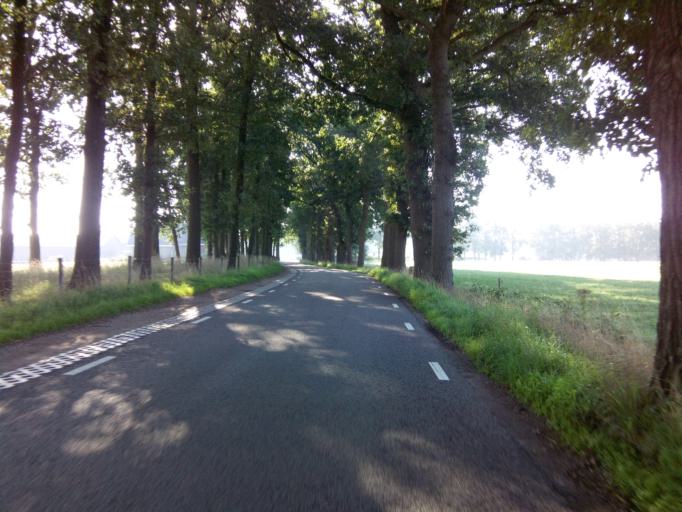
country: NL
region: Utrecht
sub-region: Gemeente Utrechtse Heuvelrug
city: Overberg
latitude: 52.0489
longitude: 5.4562
